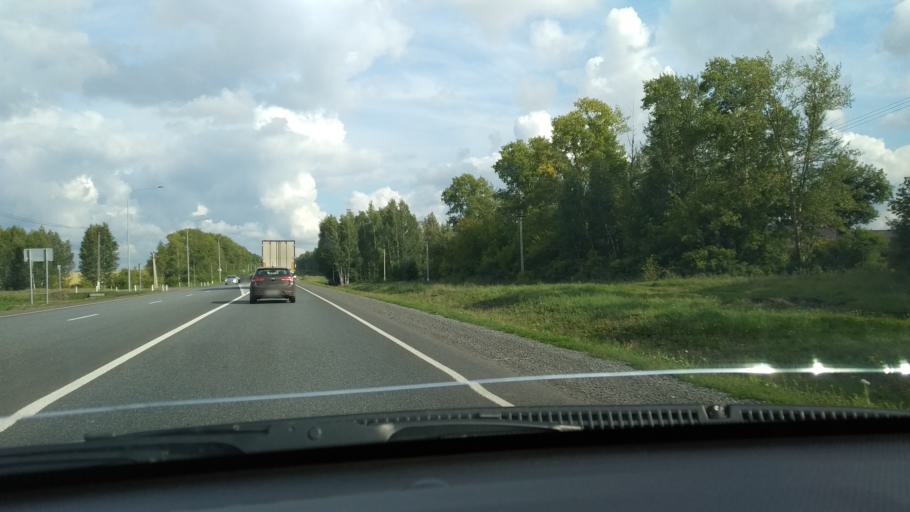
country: RU
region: Tatarstan
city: Stolbishchi
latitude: 55.6530
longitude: 49.3191
